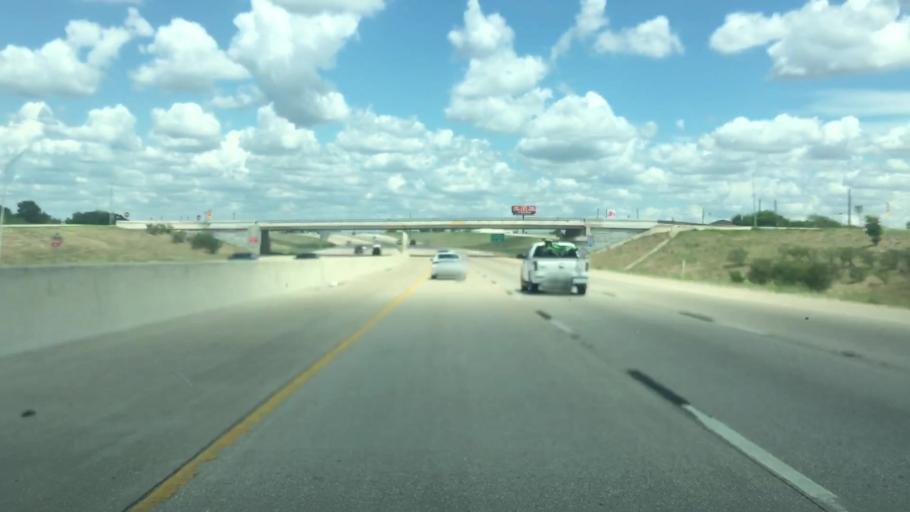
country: US
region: Texas
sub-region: Bell County
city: Salado
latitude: 30.9151
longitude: -97.5482
